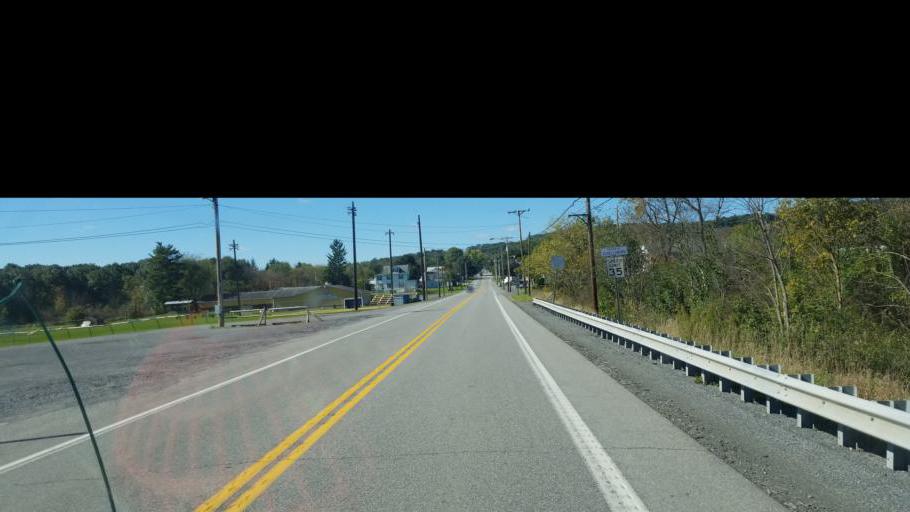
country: US
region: Pennsylvania
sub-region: Bedford County
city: Bedford
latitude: 40.0490
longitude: -78.6356
